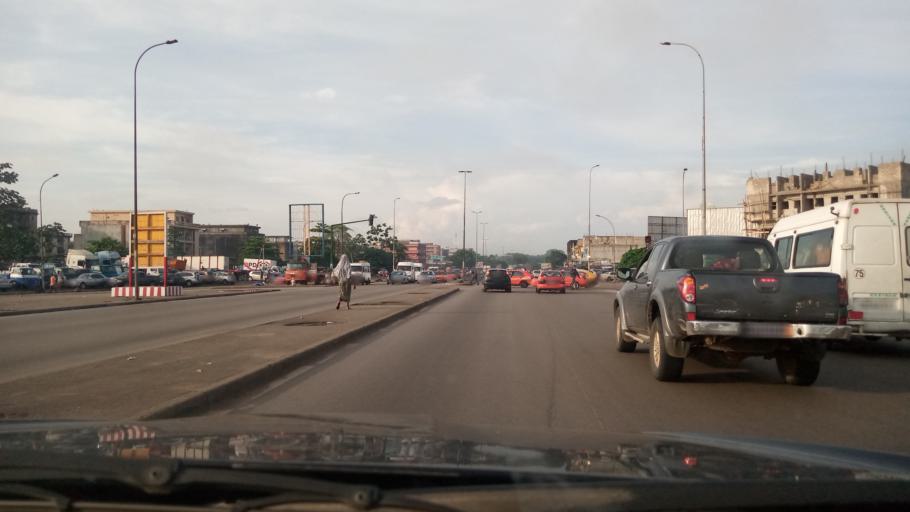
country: CI
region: Lagunes
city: Abobo
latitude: 5.4116
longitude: -4.0162
